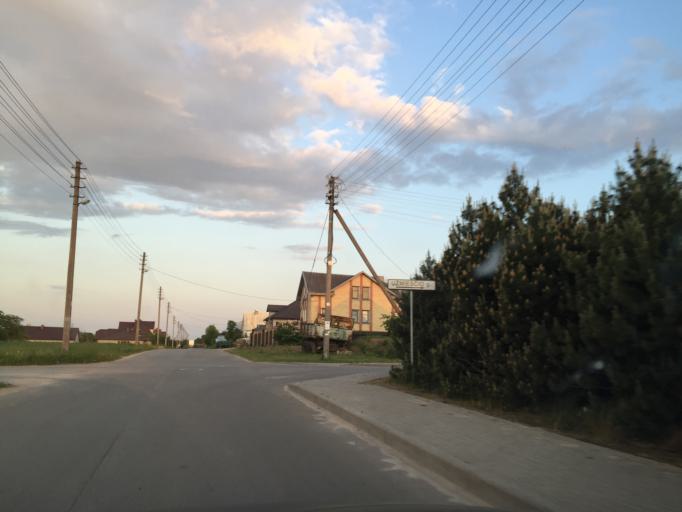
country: LT
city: Kursenai
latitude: 56.0100
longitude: 22.9539
